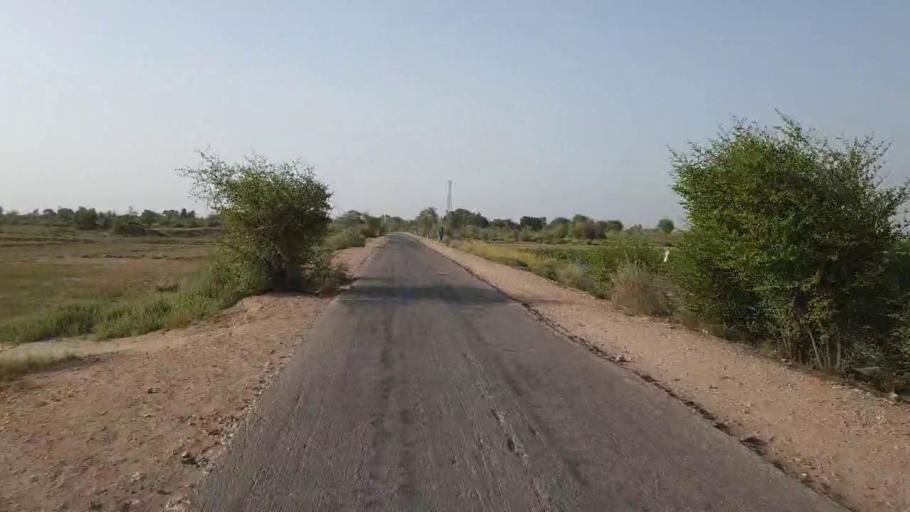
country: PK
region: Sindh
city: Jam Sahib
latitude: 26.4768
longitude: 68.8600
